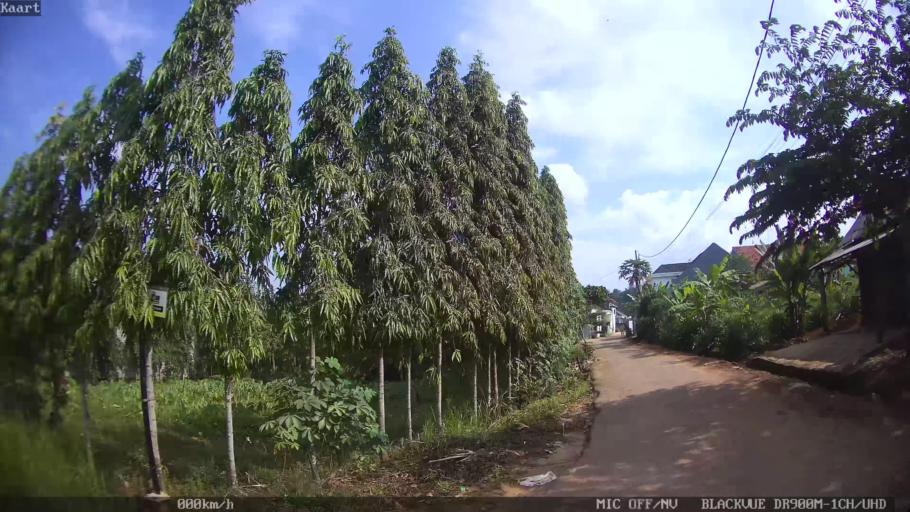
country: ID
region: Lampung
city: Kedaton
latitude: -5.3829
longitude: 105.2278
